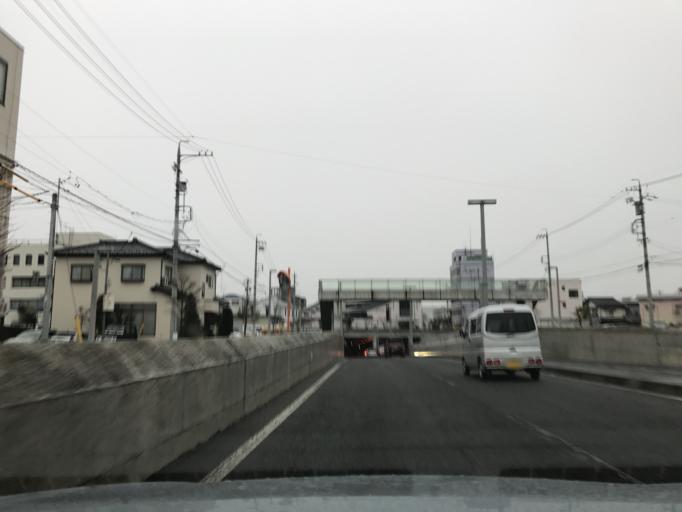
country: JP
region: Nagano
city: Matsumoto
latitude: 36.2372
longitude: 137.9632
